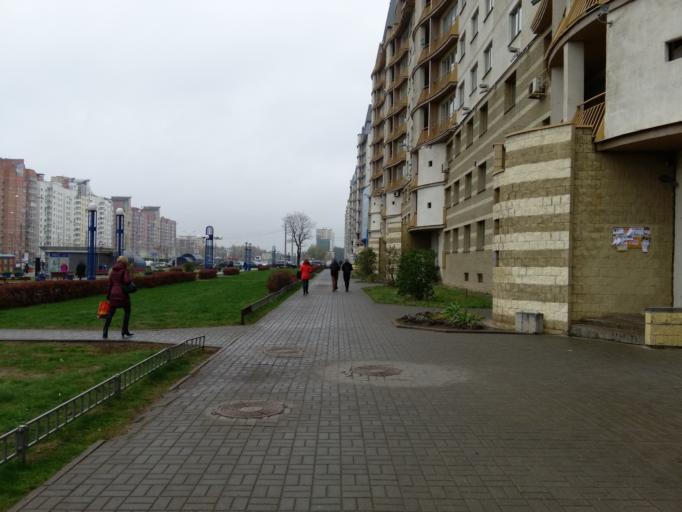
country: BY
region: Minsk
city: Borovlyany
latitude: 53.9444
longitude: 27.6877
